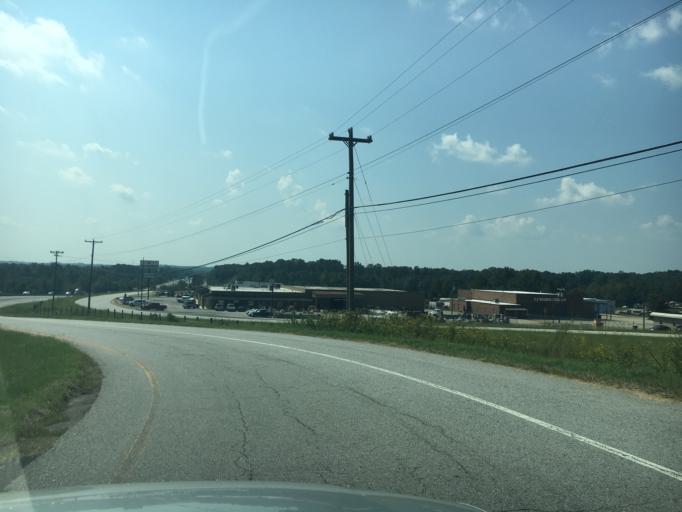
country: US
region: South Carolina
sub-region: Anderson County
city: Powdersville
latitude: 34.7605
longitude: -82.4751
